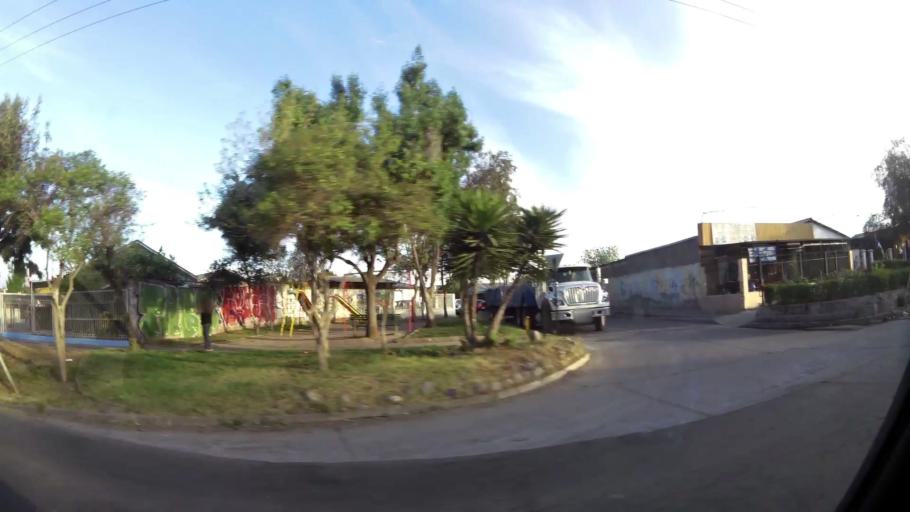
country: CL
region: Santiago Metropolitan
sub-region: Provincia de Santiago
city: Lo Prado
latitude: -33.4501
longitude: -70.7109
